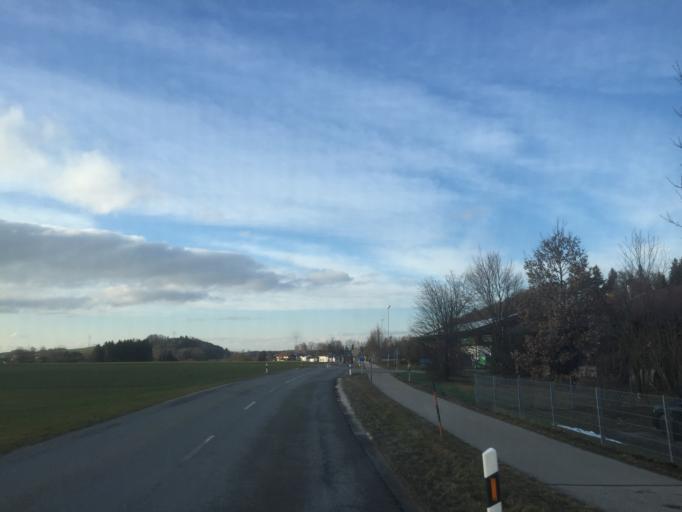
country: DE
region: Bavaria
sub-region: Upper Bavaria
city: Vachendorf
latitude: 47.8456
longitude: 12.6032
